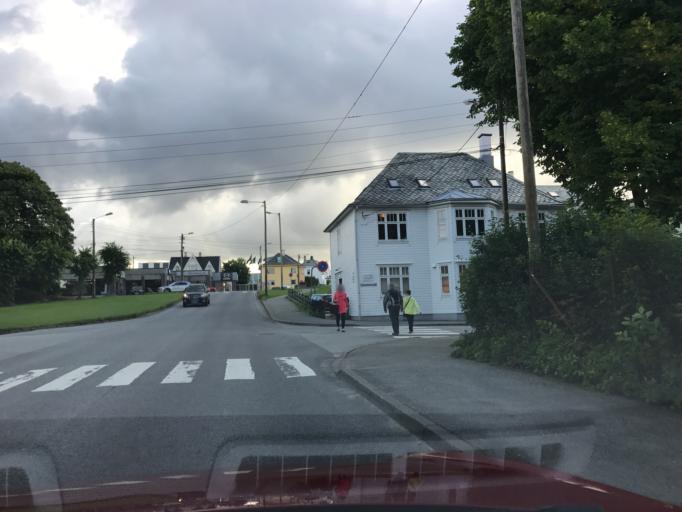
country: NO
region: Rogaland
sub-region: Haugesund
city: Haugesund
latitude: 59.4131
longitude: 5.2729
